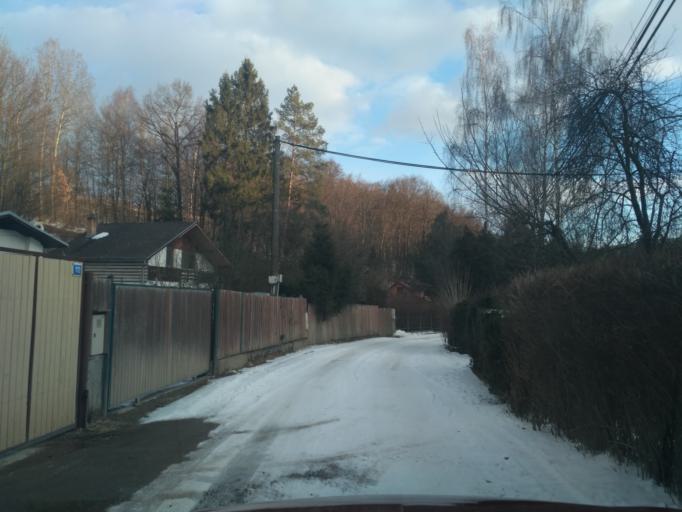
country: SK
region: Kosicky
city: Kosice
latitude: 48.7295
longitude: 21.1624
